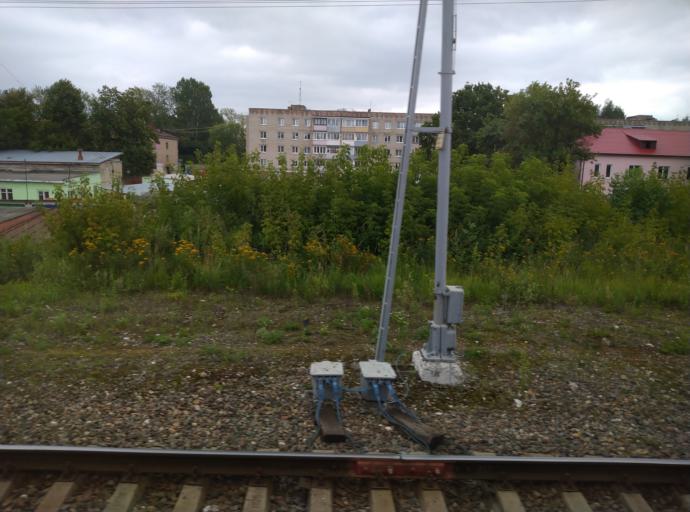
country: RU
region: Kostroma
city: Nerekhta
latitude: 57.4636
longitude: 40.5528
